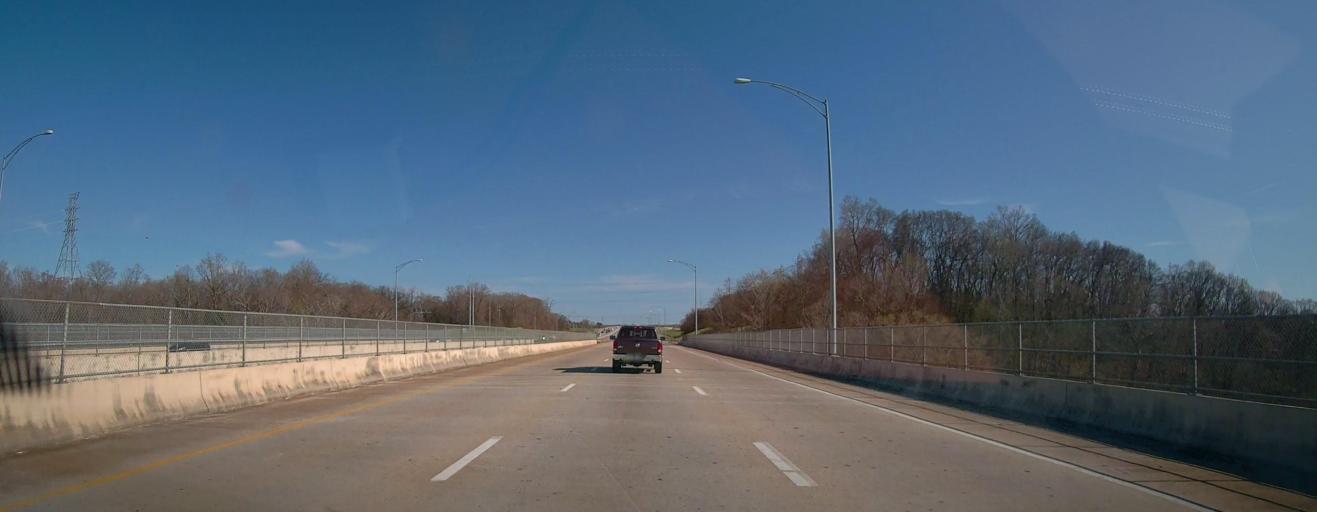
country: US
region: Alabama
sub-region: Lauderdale County
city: East Florence
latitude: 34.7917
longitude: -87.6428
